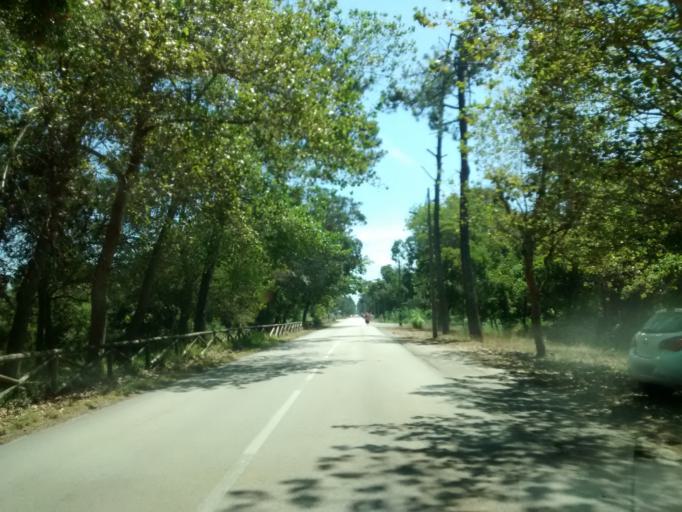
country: PT
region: Coimbra
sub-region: Mira
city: Mira
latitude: 40.4463
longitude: -8.7994
